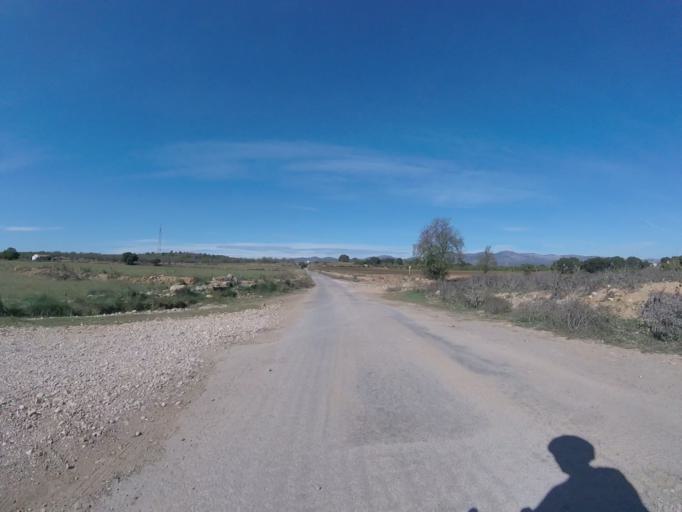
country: ES
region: Valencia
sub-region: Provincia de Castello
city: Benlloch
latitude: 40.2087
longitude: 0.0440
